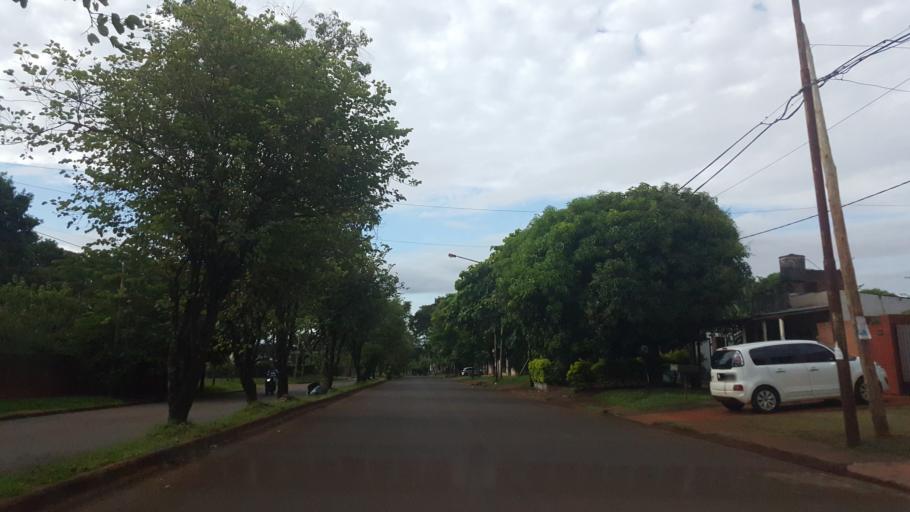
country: AR
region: Misiones
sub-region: Departamento de Capital
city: Posadas
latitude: -27.3997
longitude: -55.9362
